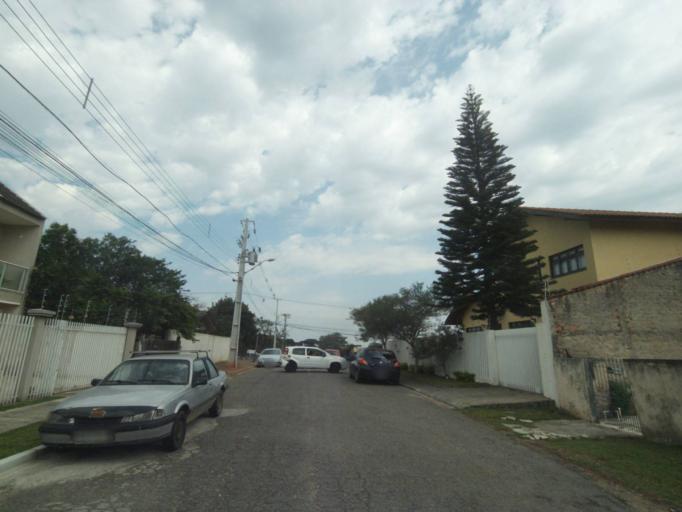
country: BR
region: Parana
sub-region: Sao Jose Dos Pinhais
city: Sao Jose dos Pinhais
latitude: -25.5242
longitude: -49.2556
